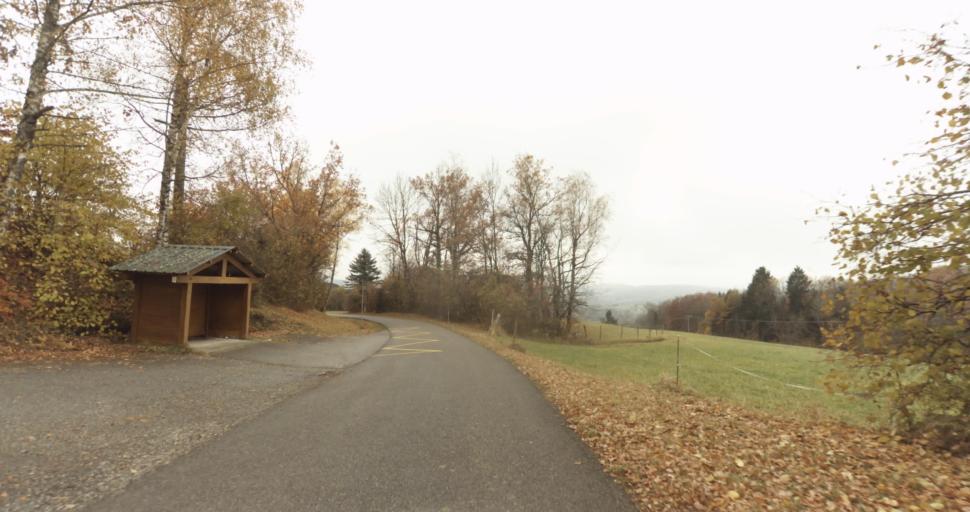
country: FR
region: Rhone-Alpes
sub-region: Departement de la Haute-Savoie
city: Groisy
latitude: 46.0232
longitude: 6.1975
